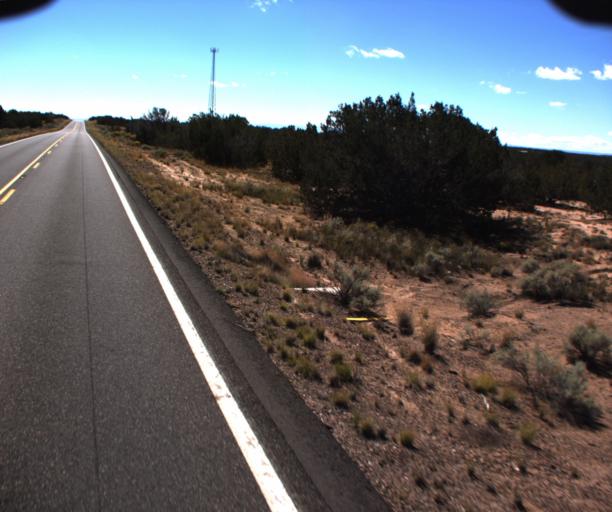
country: US
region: Arizona
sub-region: Apache County
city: Saint Johns
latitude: 34.8470
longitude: -109.2376
